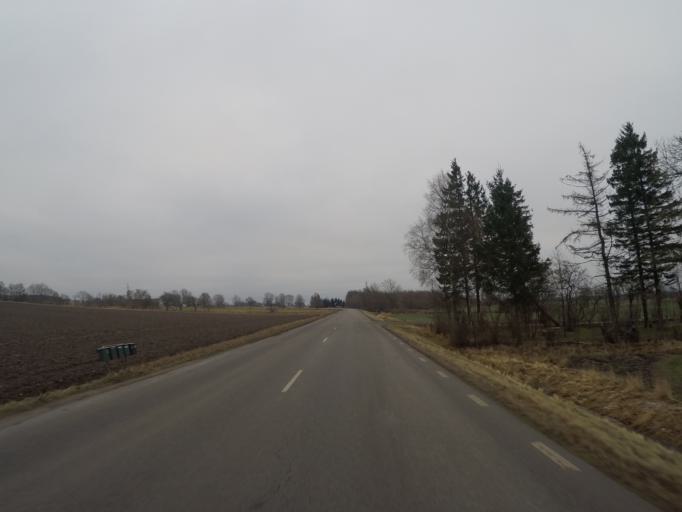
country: SE
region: Skane
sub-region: Hoors Kommun
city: Loberod
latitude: 55.7716
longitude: 13.4389
